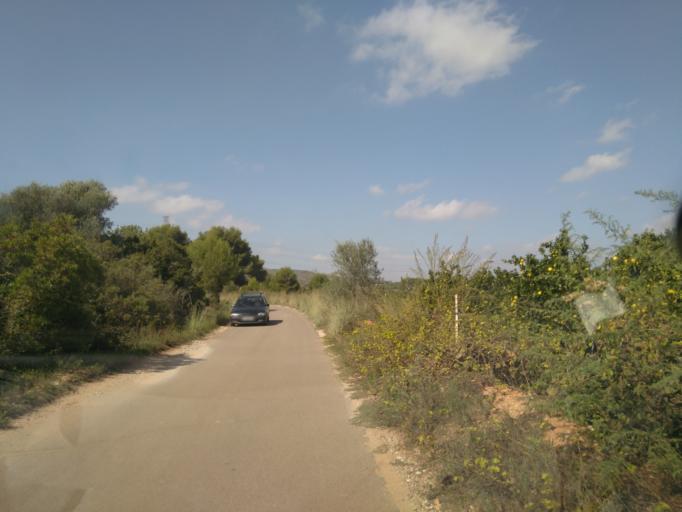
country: ES
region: Valencia
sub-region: Provincia de Valencia
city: Tous
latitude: 39.1746
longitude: -0.5938
